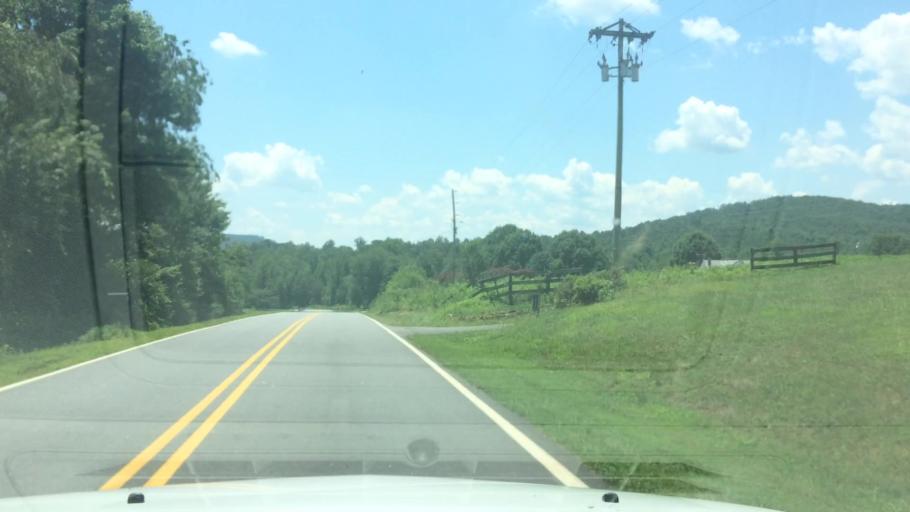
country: US
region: North Carolina
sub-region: Alexander County
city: Taylorsville
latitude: 35.9497
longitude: -81.2672
